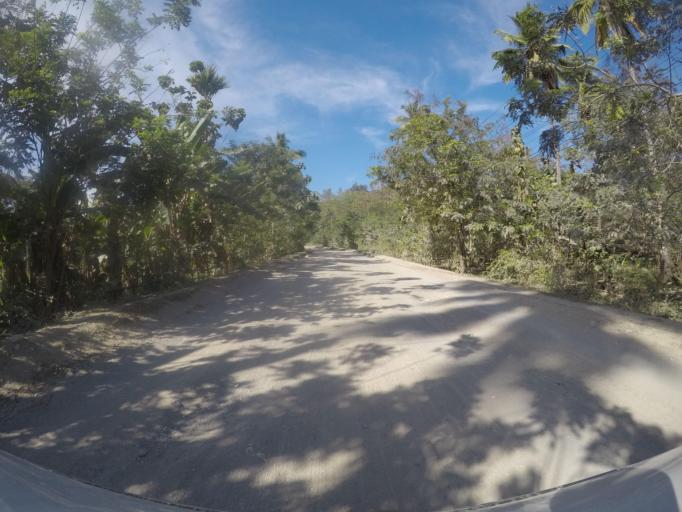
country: TL
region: Viqueque
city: Viqueque
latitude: -8.8426
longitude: 126.3696
